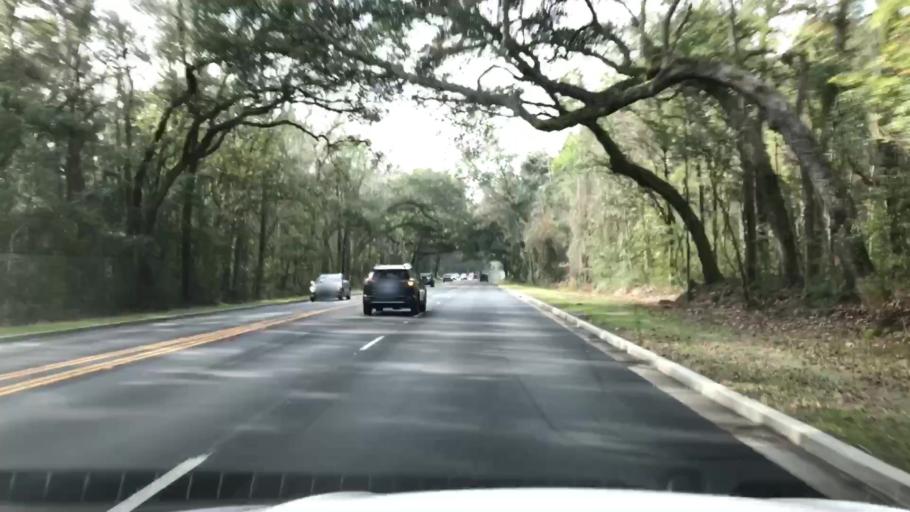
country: US
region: South Carolina
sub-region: Charleston County
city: Shell Point
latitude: 32.7471
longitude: -80.0345
